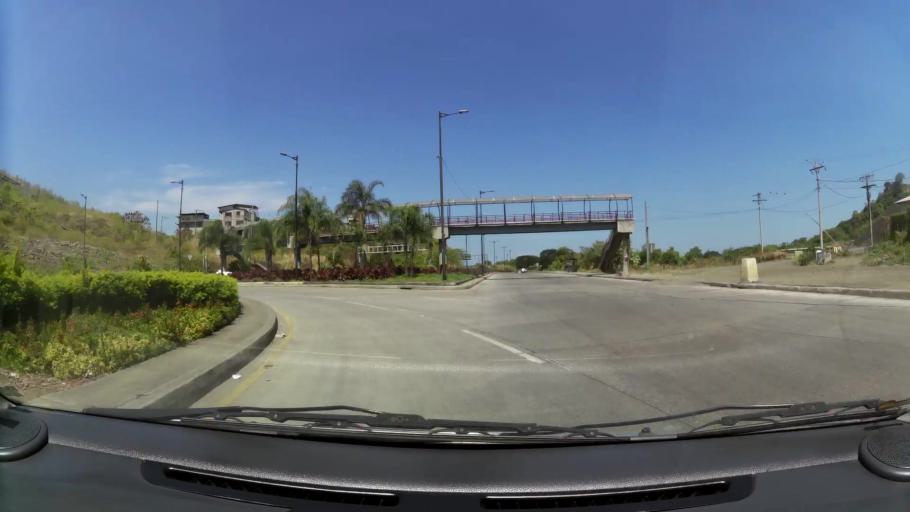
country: EC
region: Guayas
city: Guayaquil
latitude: -2.1852
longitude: -79.9322
